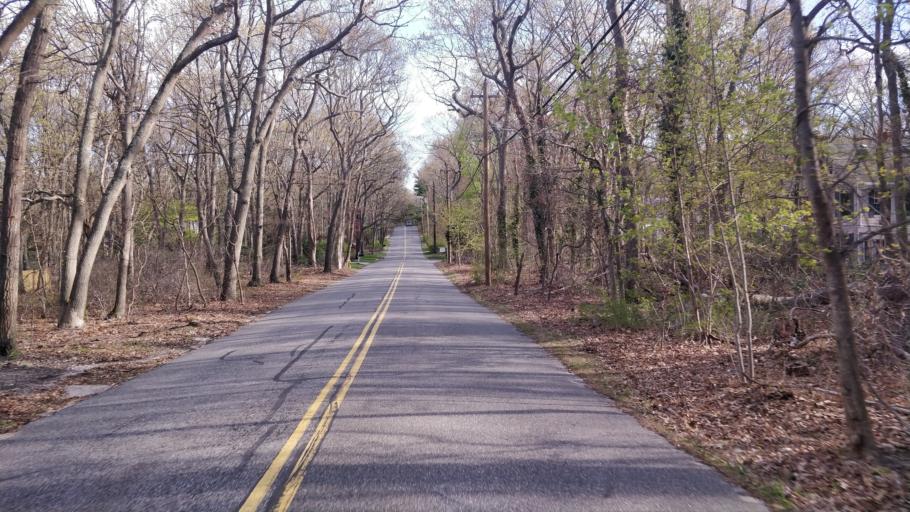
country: US
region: New York
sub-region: Suffolk County
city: Stony Brook
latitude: 40.9528
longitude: -73.1365
